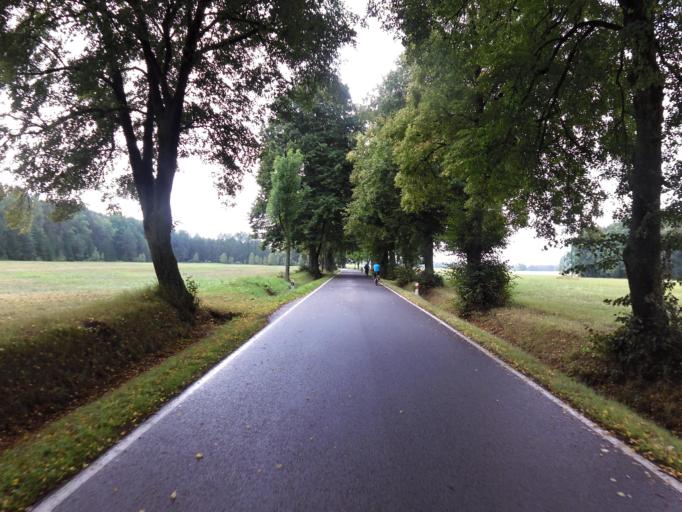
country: CZ
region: Jihocesky
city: Chlum u Trebone
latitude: 48.9172
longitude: 14.9195
